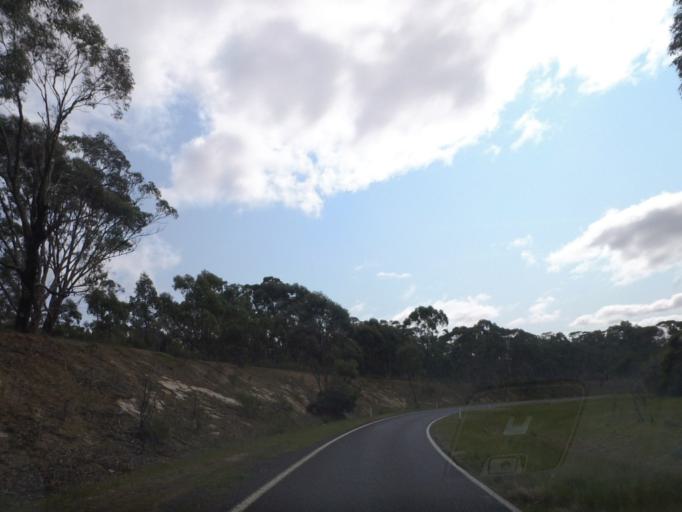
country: AU
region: Victoria
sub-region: Murrindindi
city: Kinglake West
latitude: -37.1093
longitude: 145.0903
